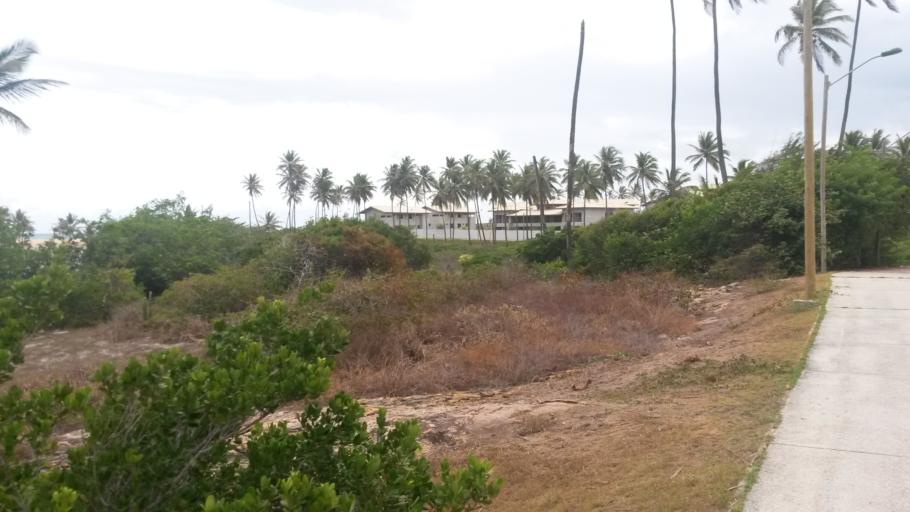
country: BR
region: Bahia
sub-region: Mata De Sao Joao
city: Mata de Sao Joao
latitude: -12.4977
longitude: -37.9613
